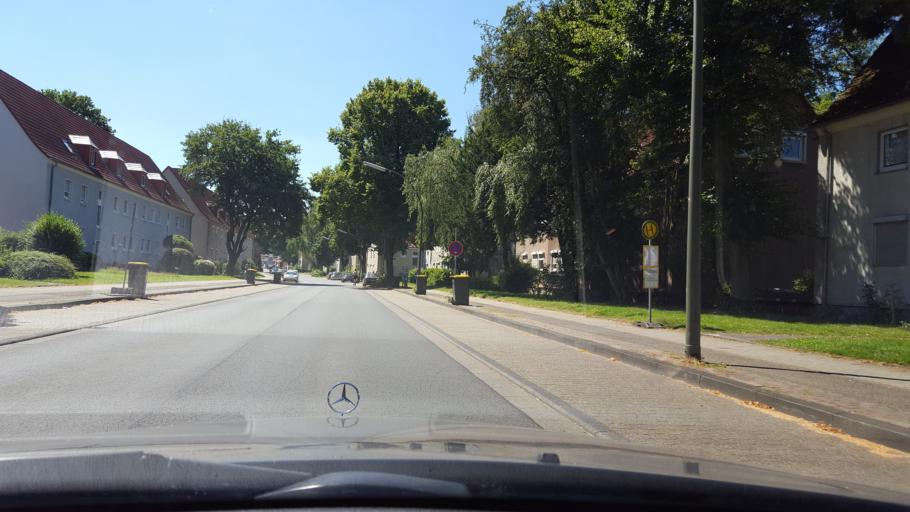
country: DE
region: North Rhine-Westphalia
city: Marl
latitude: 51.6579
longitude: 7.1112
